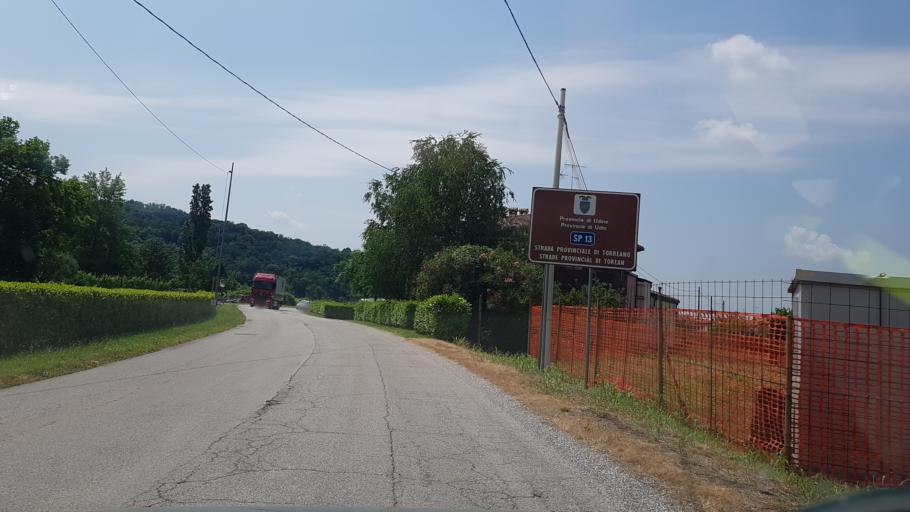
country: IT
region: Friuli Venezia Giulia
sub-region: Provincia di Udine
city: Torreano
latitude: 46.1220
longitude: 13.4230
